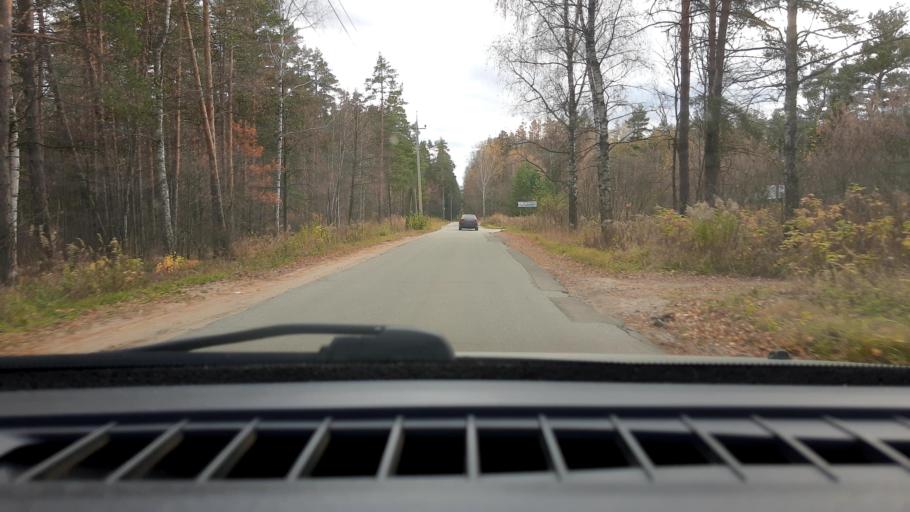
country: RU
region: Nizjnij Novgorod
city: Afonino
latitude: 56.1714
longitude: 44.0972
